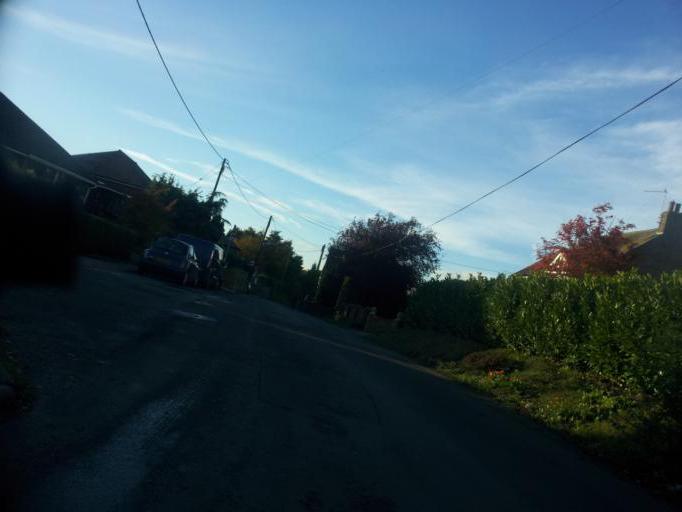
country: GB
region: England
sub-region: Kent
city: Newington
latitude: 51.3564
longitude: 0.6708
